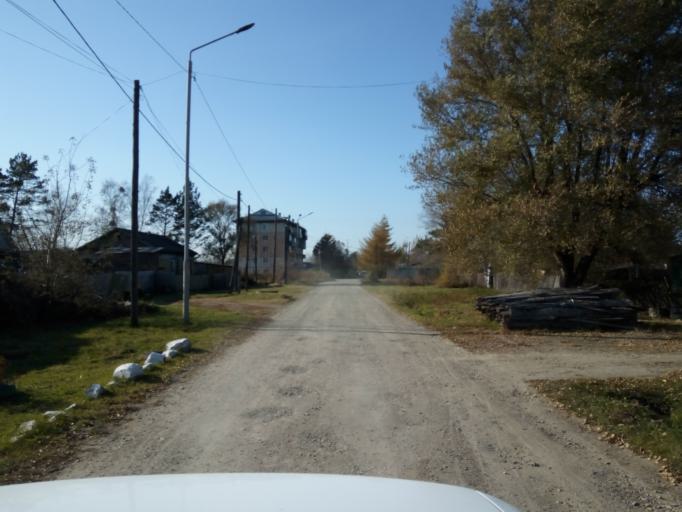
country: RU
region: Primorskiy
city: Dal'nerechensk
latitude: 45.9212
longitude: 133.7438
